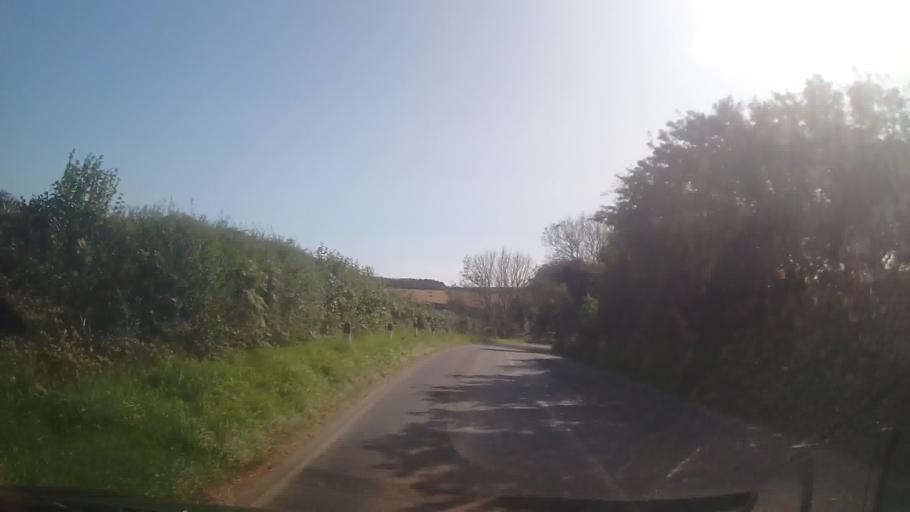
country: GB
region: Wales
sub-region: Pembrokeshire
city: Mathry
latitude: 51.9377
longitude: -5.0439
